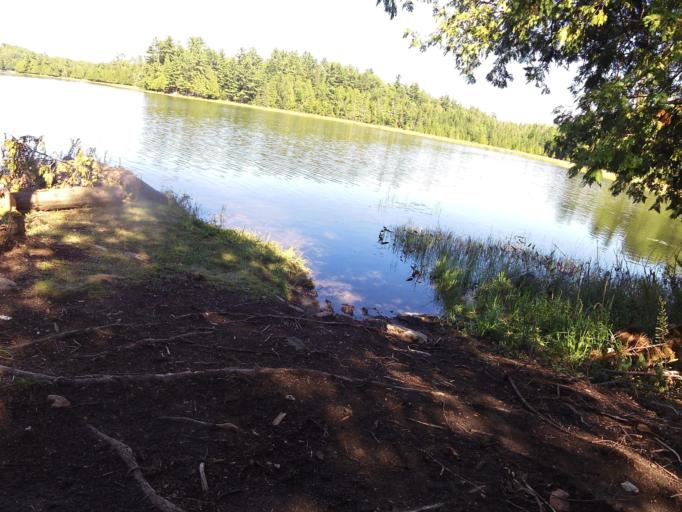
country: CA
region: Ontario
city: Renfrew
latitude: 45.1326
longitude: -76.7303
